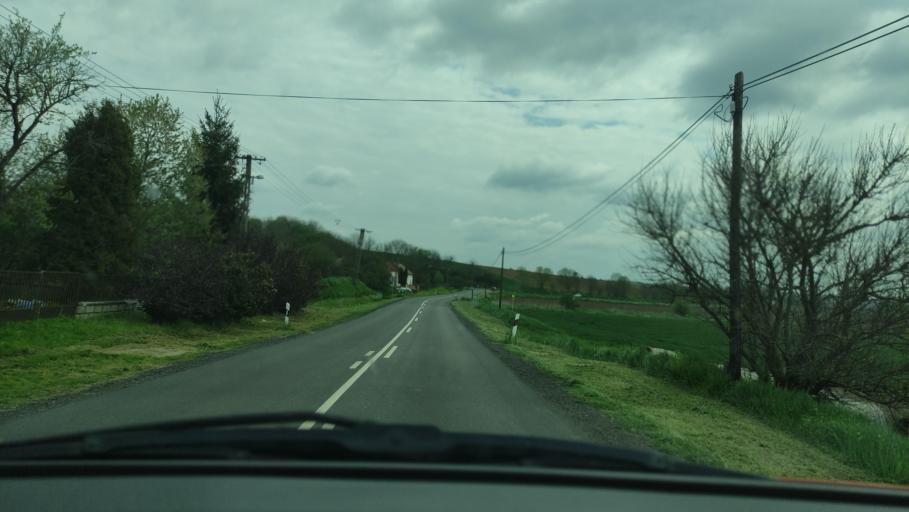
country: HU
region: Baranya
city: Sasd
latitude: 46.2646
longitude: 18.0856
